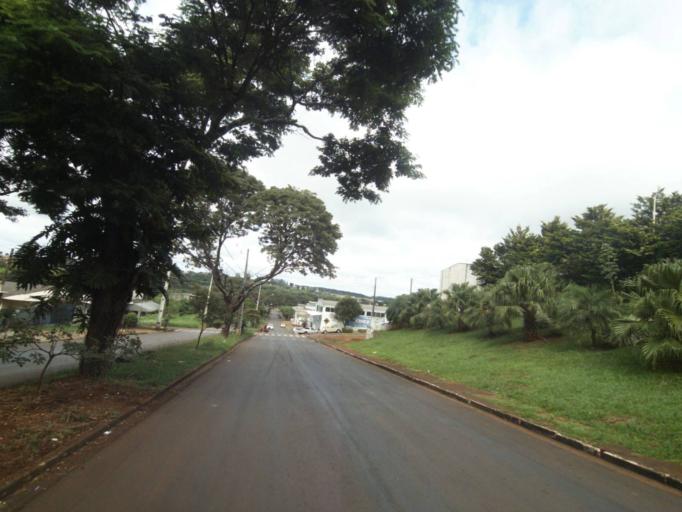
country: BR
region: Parana
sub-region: Campo Mourao
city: Campo Mourao
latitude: -24.0512
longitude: -52.3796
